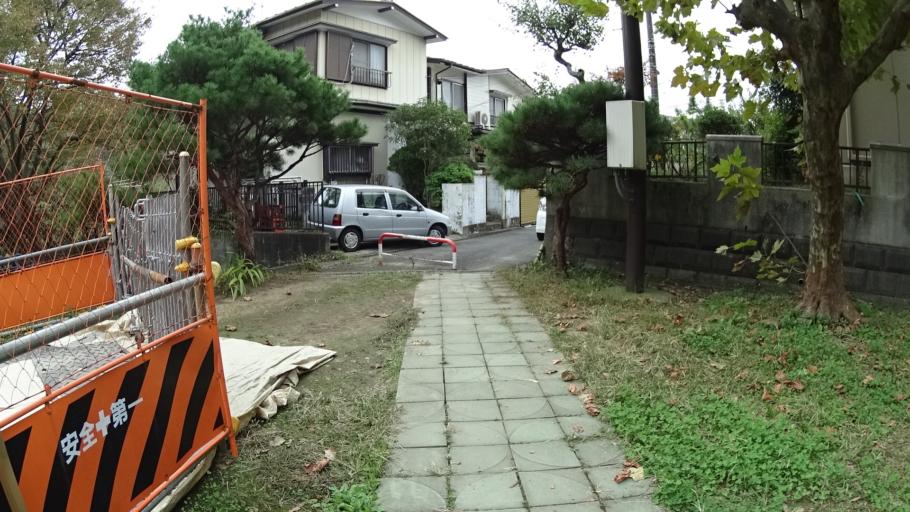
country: JP
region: Kanagawa
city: Zushi
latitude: 35.2979
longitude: 139.6193
